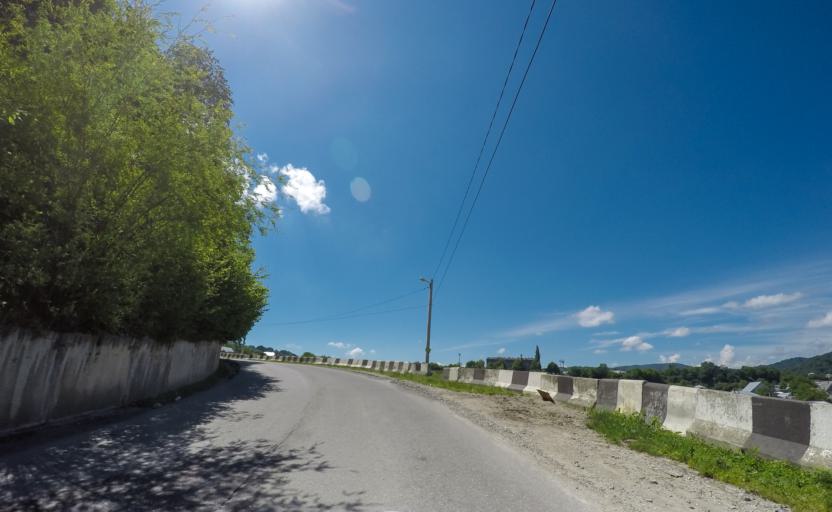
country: RU
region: Kabardino-Balkariya
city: Belaya Rechka
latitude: 43.4367
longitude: 43.5774
